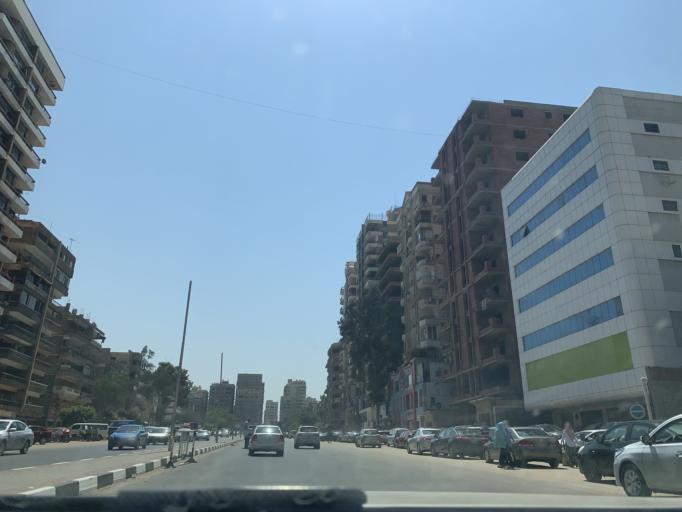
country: EG
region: Muhafazat al Qahirah
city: Cairo
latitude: 30.0528
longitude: 31.3464
